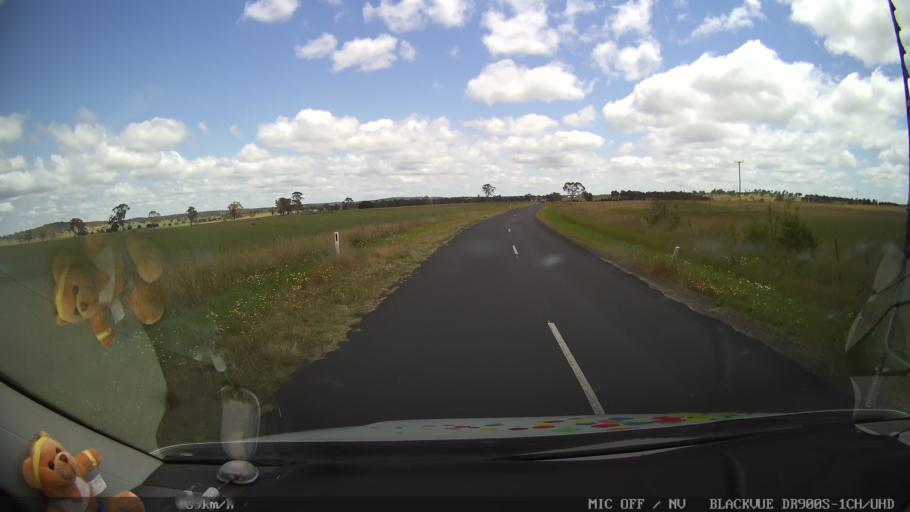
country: AU
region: New South Wales
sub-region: Glen Innes Severn
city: Glen Innes
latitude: -29.6600
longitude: 151.6924
